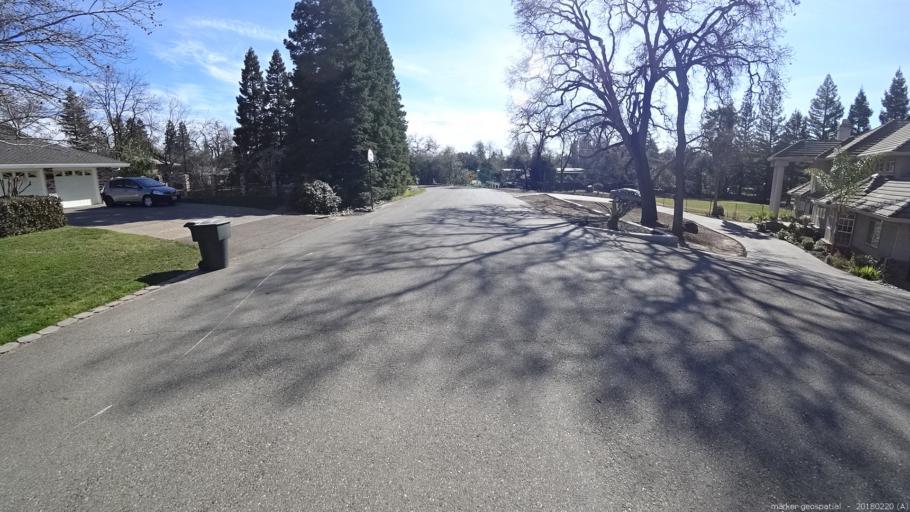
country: US
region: California
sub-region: Sacramento County
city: Orangevale
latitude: 38.6937
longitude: -121.2376
